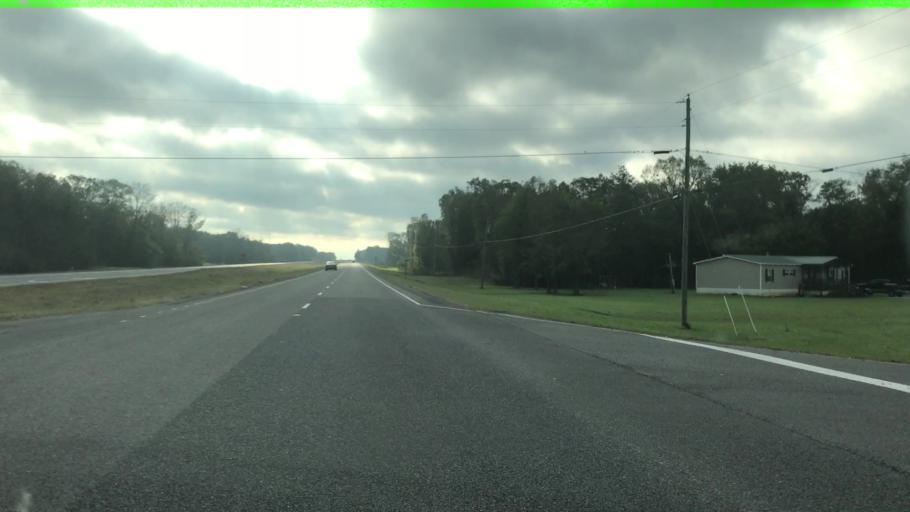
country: US
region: Alabama
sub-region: Morgan County
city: Danville
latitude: 34.4099
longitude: -87.1493
